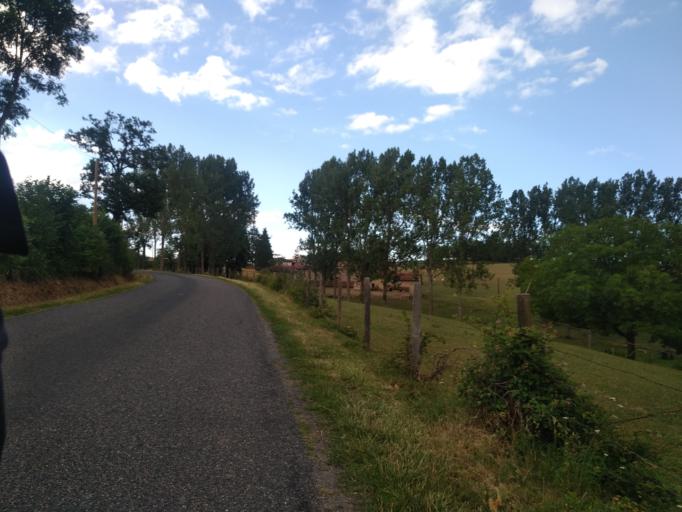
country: FR
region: Rhone-Alpes
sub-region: Departement de la Loire
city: Panissieres
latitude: 45.7445
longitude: 4.3495
